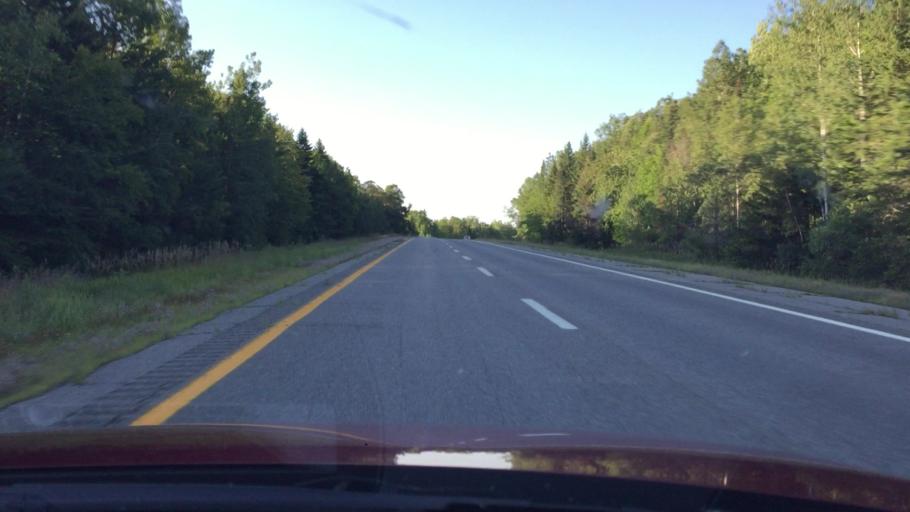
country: US
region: Maine
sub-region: Penobscot County
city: Patten
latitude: 45.8353
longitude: -68.4328
